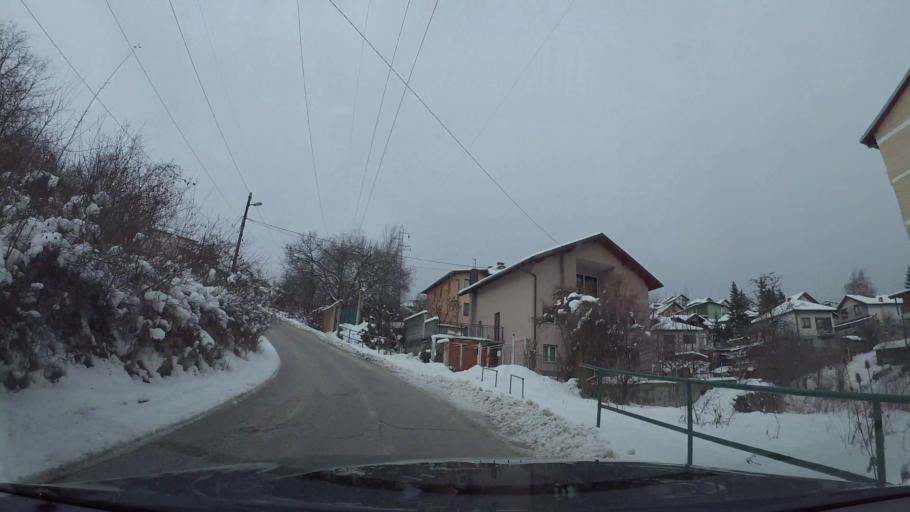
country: BA
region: Federation of Bosnia and Herzegovina
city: Kobilja Glava
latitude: 43.8659
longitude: 18.3968
